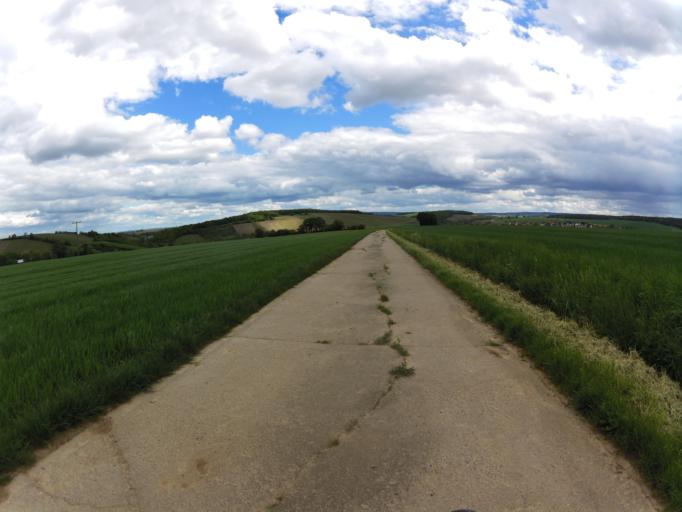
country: DE
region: Bavaria
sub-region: Regierungsbezirk Unterfranken
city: Volkach
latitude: 49.8774
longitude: 10.2418
